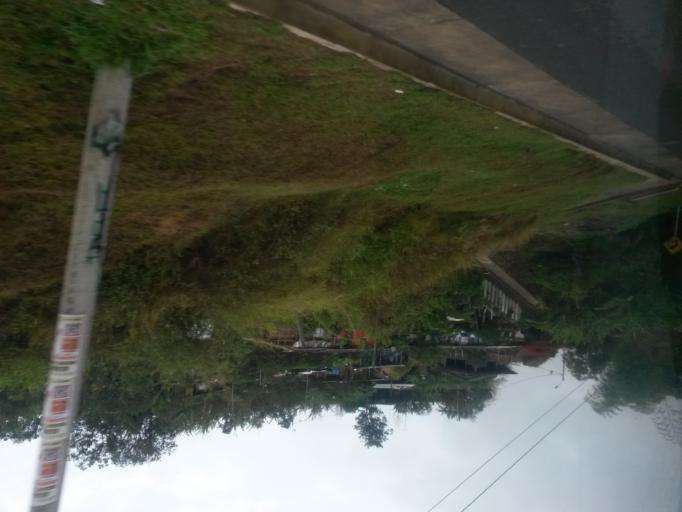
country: CO
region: Cauca
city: Popayan
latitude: 2.4246
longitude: -76.6235
